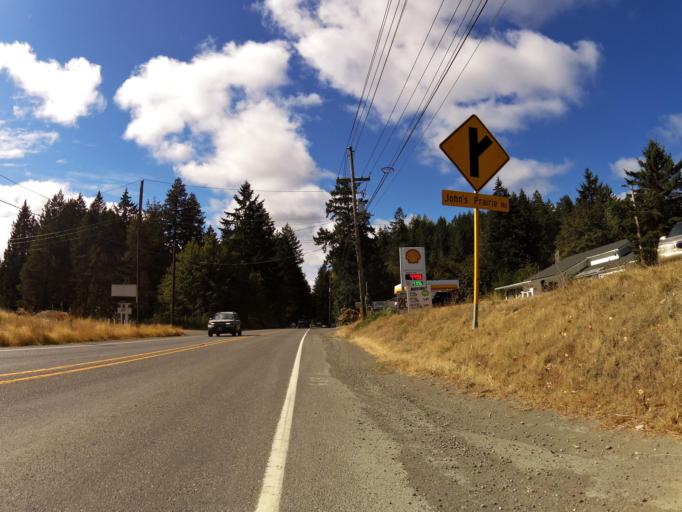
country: US
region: Washington
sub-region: Mason County
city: Shelton
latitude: 47.2492
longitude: -123.0441
